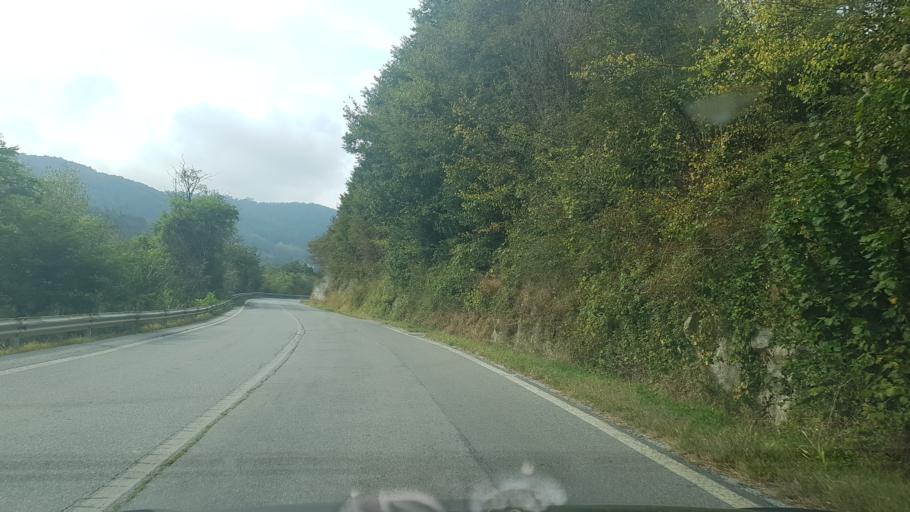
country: IT
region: Piedmont
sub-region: Provincia di Cuneo
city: Monesiglio
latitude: 44.4495
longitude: 8.1355
